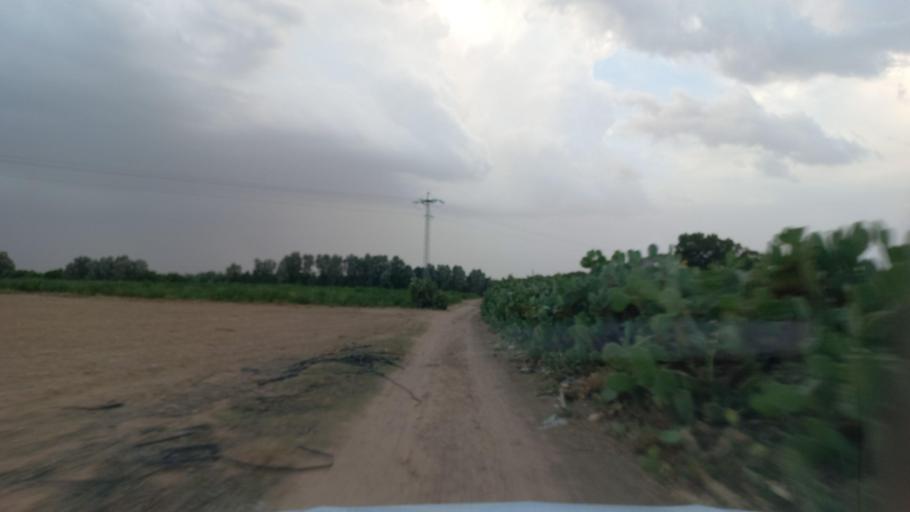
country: TN
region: Al Qasrayn
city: Kasserine
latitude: 35.2744
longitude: 9.0579
